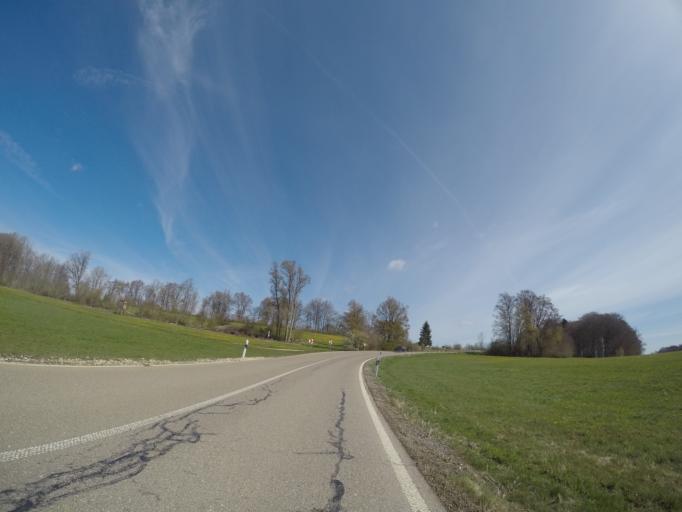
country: DE
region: Baden-Wuerttemberg
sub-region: Regierungsbezirk Stuttgart
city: Wiesensteig
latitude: 48.5386
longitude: 9.6228
